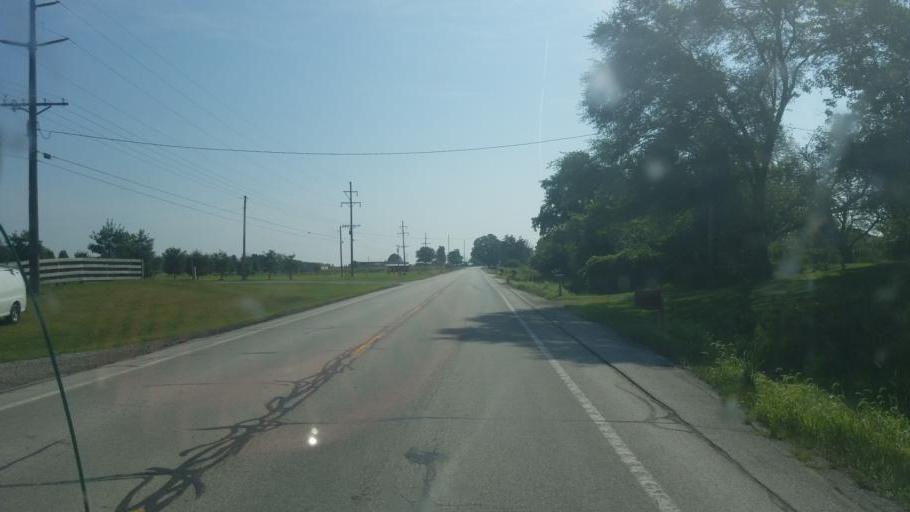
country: US
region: Ohio
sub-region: Wayne County
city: West Salem
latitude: 41.0284
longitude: -82.1786
